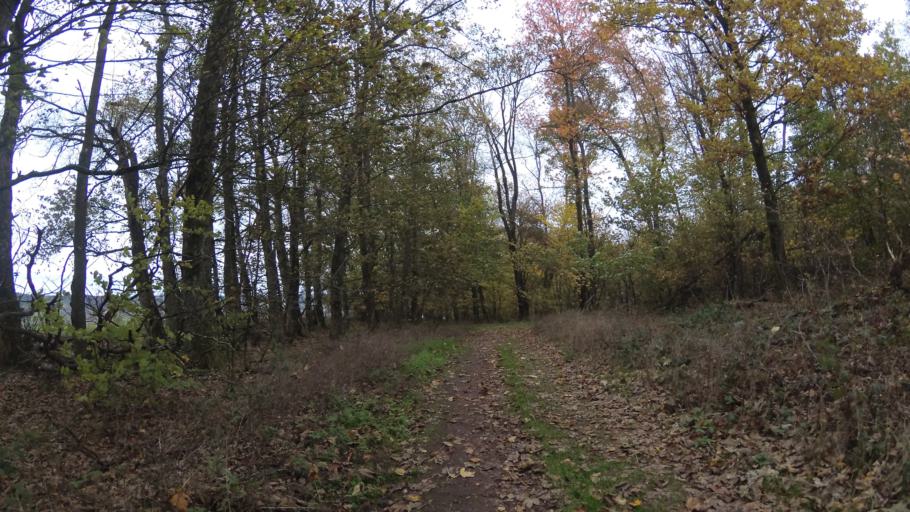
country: DE
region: Saarland
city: Sankt Wendel
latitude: 49.4585
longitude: 7.1956
